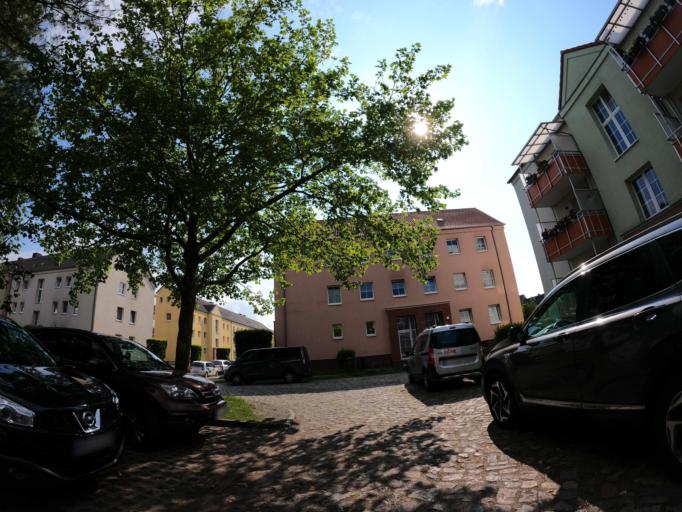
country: DE
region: Mecklenburg-Vorpommern
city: Stralsund
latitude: 54.3059
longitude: 13.0675
